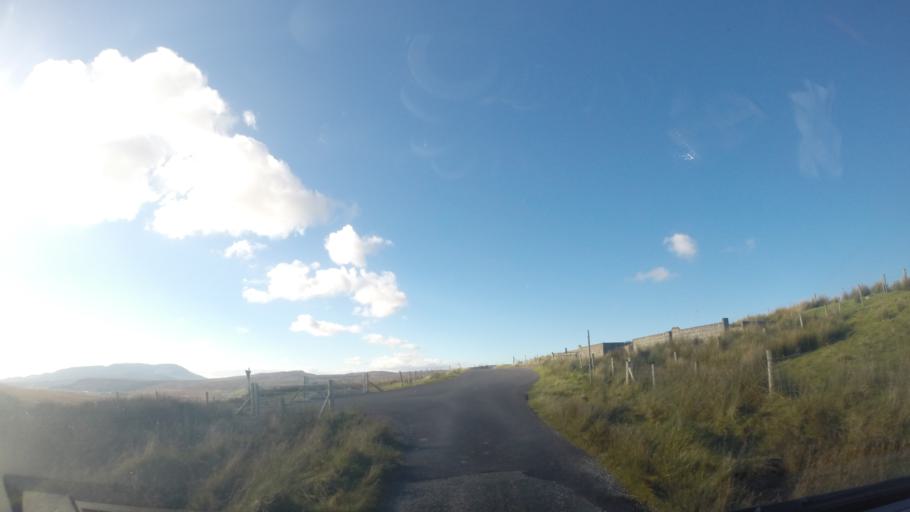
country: IE
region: Ulster
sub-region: County Donegal
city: Killybegs
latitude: 54.7217
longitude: -8.5809
